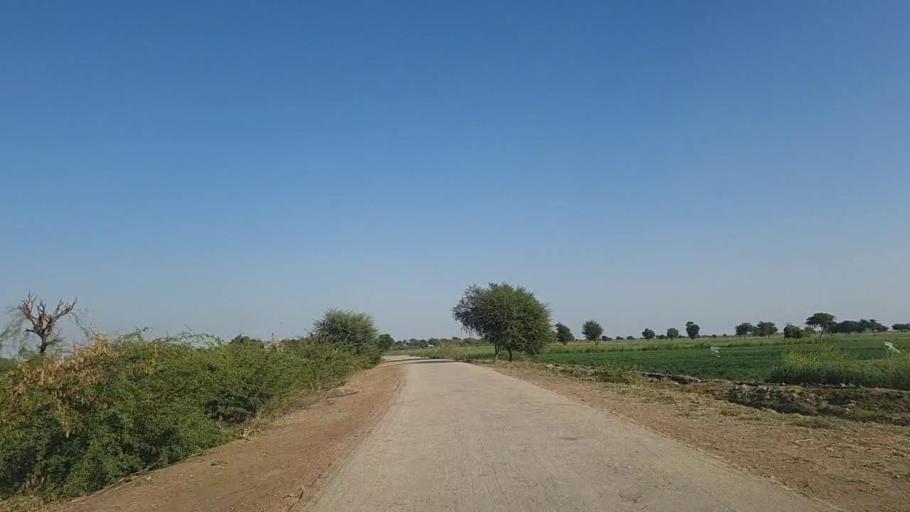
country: PK
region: Sindh
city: Naukot
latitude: 24.9455
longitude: 69.3454
